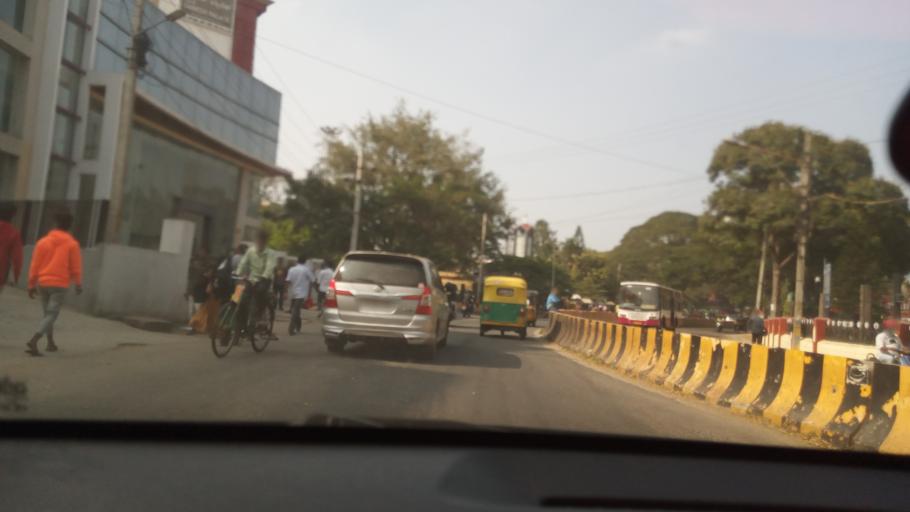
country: IN
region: Karnataka
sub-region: Mysore
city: Mysore
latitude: 12.3099
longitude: 76.6588
